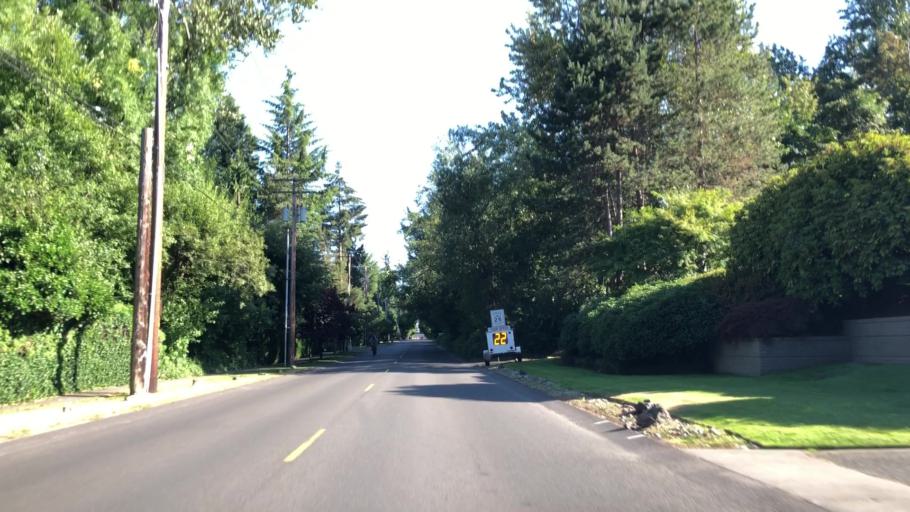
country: US
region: Washington
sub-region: King County
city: Medina
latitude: 47.6343
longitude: -122.2386
